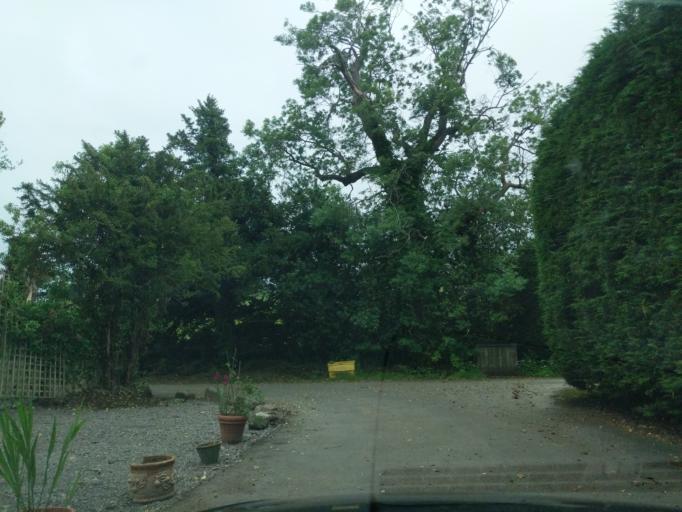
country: GB
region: Scotland
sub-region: Edinburgh
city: Currie
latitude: 55.9017
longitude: -3.2834
